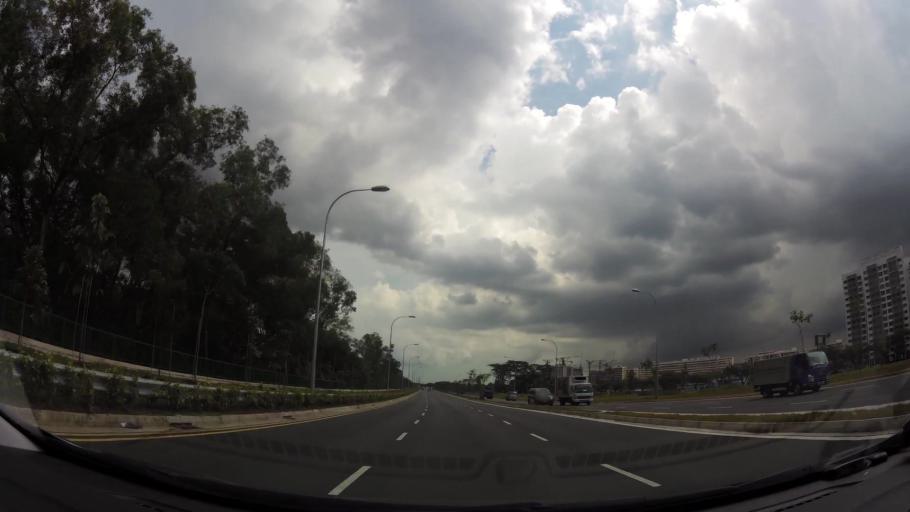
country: MY
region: Johor
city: Kampung Pasir Gudang Baru
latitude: 1.4342
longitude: 103.8473
